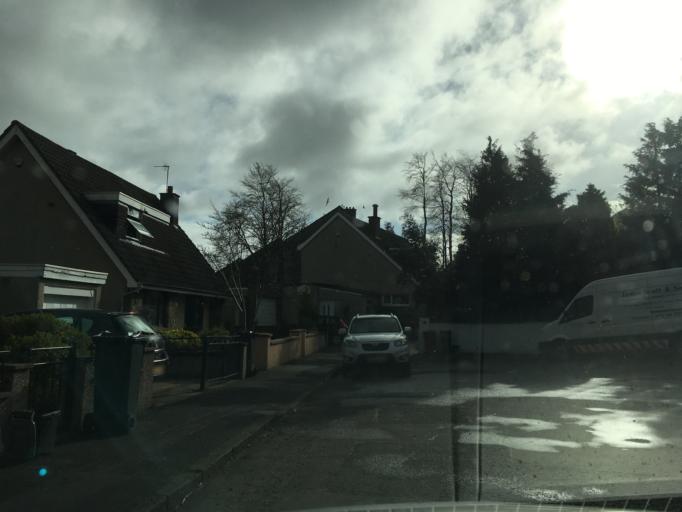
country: GB
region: Scotland
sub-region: Edinburgh
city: Colinton
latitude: 55.9057
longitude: -3.2305
